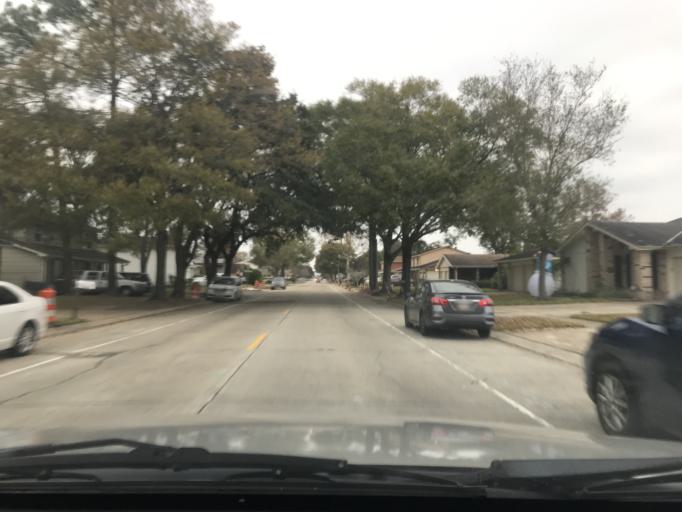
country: US
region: Louisiana
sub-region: Jefferson Parish
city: Woodmere
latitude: 29.8620
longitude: -90.0794
